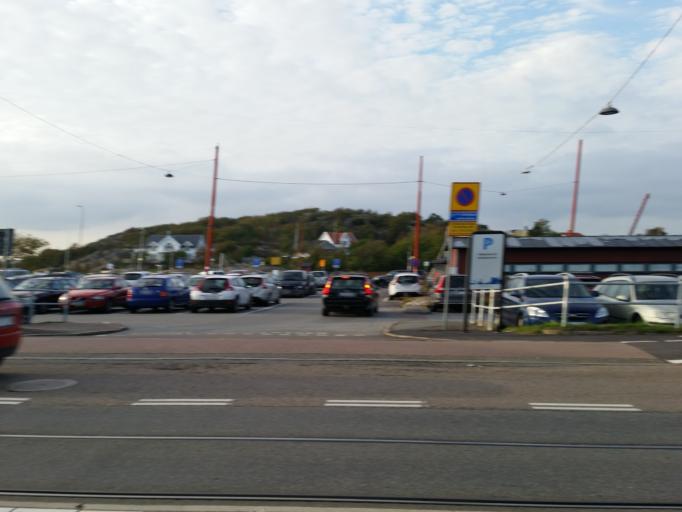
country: SE
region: Vaestra Goetaland
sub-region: Goteborg
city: Styrso
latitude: 57.6610
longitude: 11.8463
